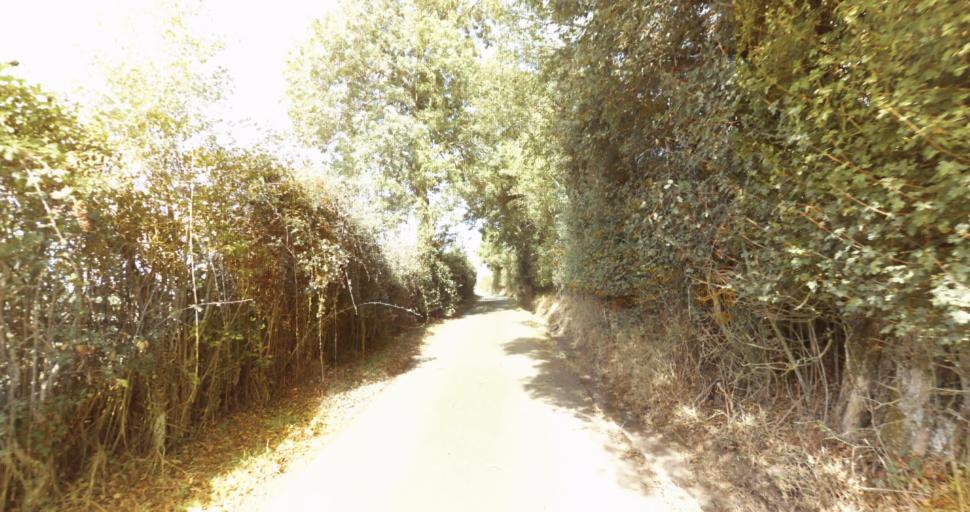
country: FR
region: Lower Normandy
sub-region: Departement de l'Orne
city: Gace
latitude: 48.7140
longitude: 0.2217
